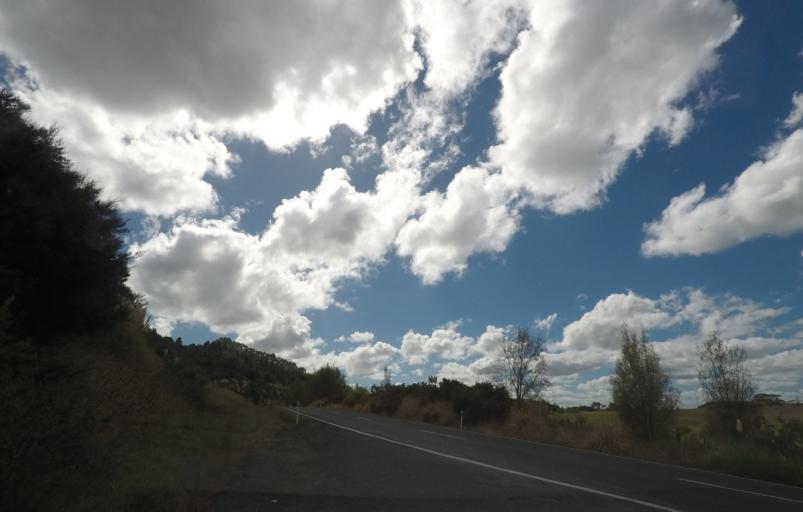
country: NZ
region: Auckland
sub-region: Auckland
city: Wellsford
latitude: -36.3366
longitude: 174.3832
